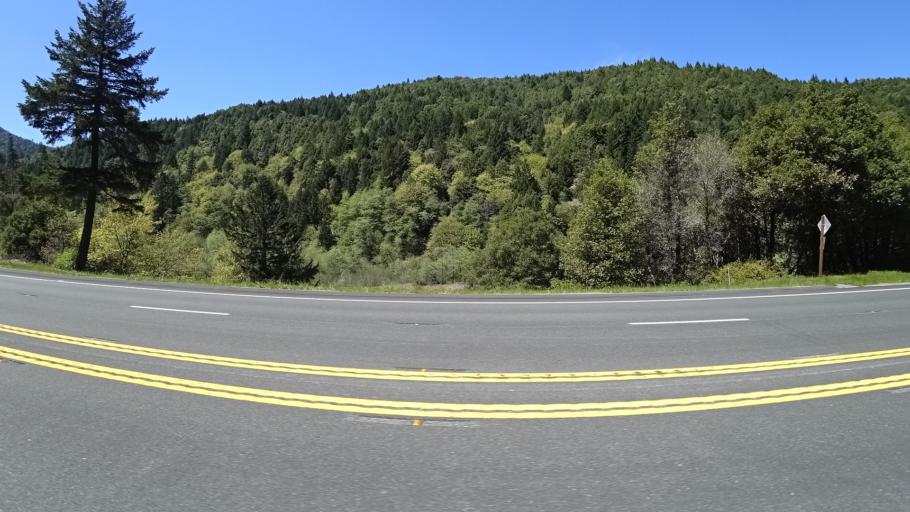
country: US
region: California
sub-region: Humboldt County
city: Willow Creek
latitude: 40.9134
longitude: -123.7043
